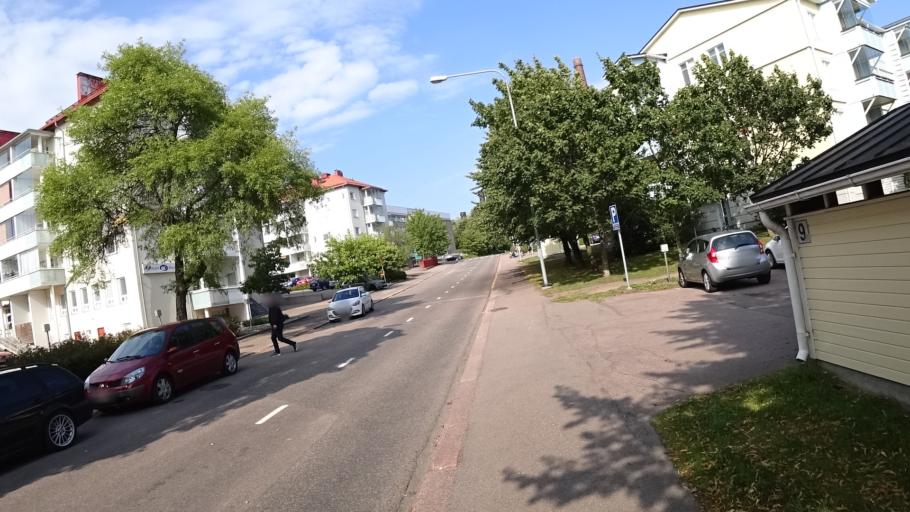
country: FI
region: Kymenlaakso
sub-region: Kotka-Hamina
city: Kotka
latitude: 60.4637
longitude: 26.9520
